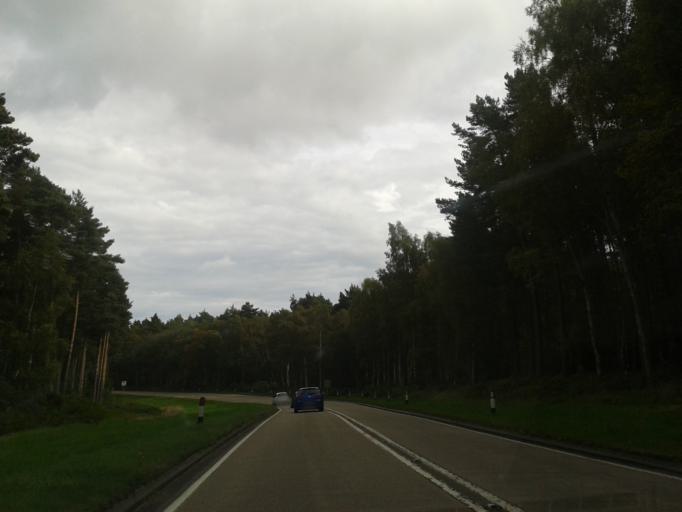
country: GB
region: Scotland
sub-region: Moray
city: Fochabers
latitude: 57.6175
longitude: -3.0643
